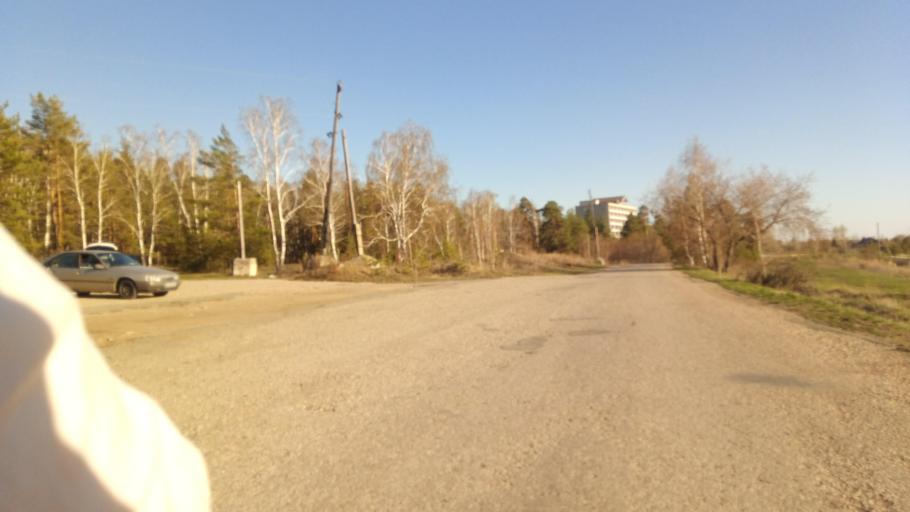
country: RU
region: Chelyabinsk
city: Novosineglazovskiy
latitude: 55.1273
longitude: 61.3284
